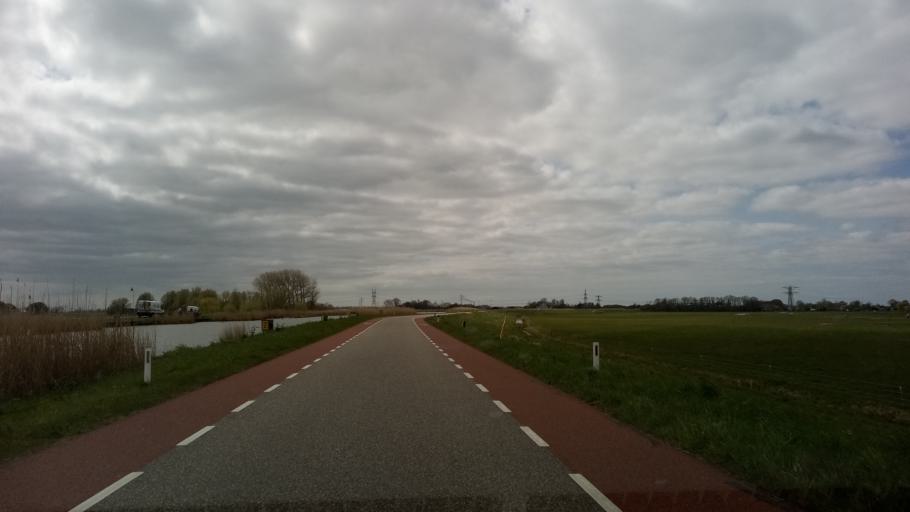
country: NL
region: North Holland
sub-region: Gemeente Heerhugowaard
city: Heerhugowaard
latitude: 52.6343
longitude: 4.8527
